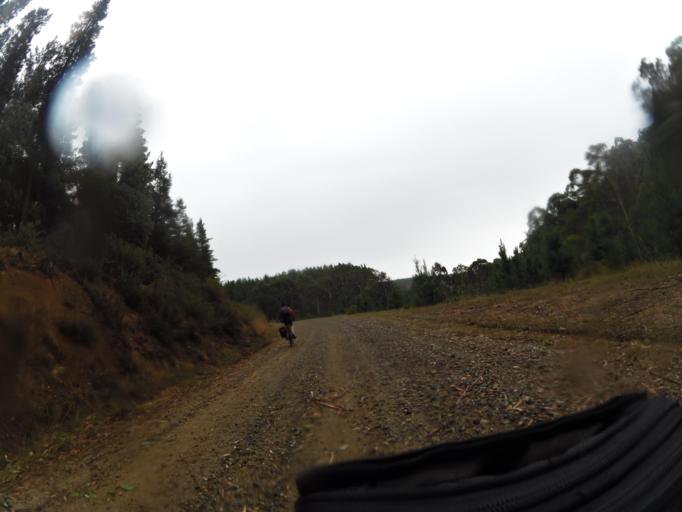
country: AU
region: New South Wales
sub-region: Greater Hume Shire
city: Holbrook
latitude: -36.2096
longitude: 147.5724
